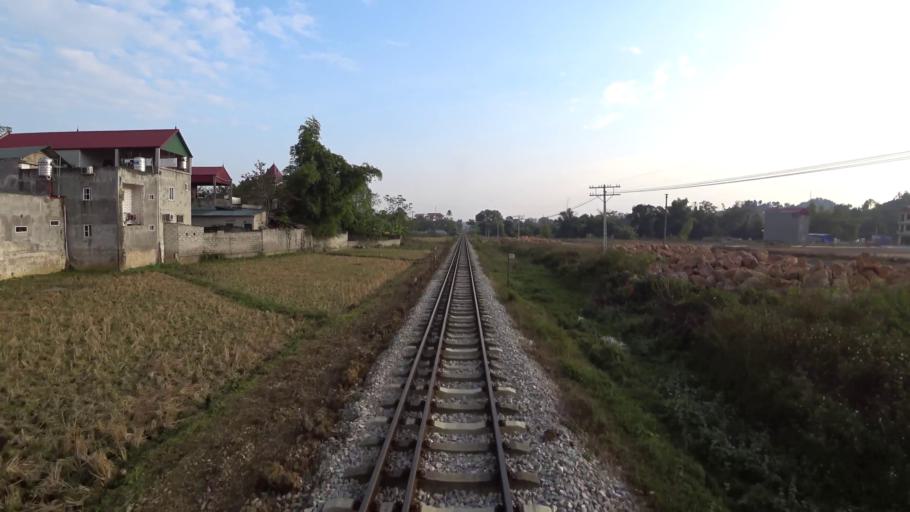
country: VN
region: Lang Son
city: Thi Tran Cao Loc
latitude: 21.8849
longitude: 106.7468
